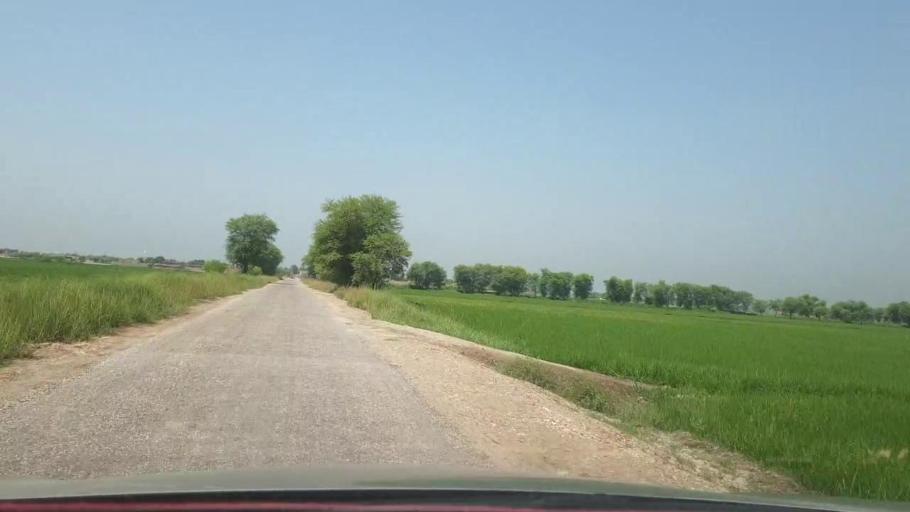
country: PK
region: Sindh
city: Kambar
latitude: 27.6114
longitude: 67.8766
